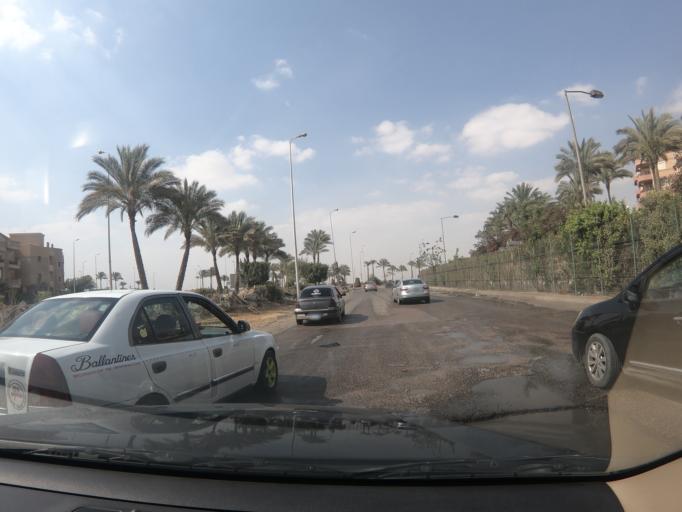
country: EG
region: Muhafazat al Qalyubiyah
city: Al Khankah
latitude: 30.0691
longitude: 31.4748
